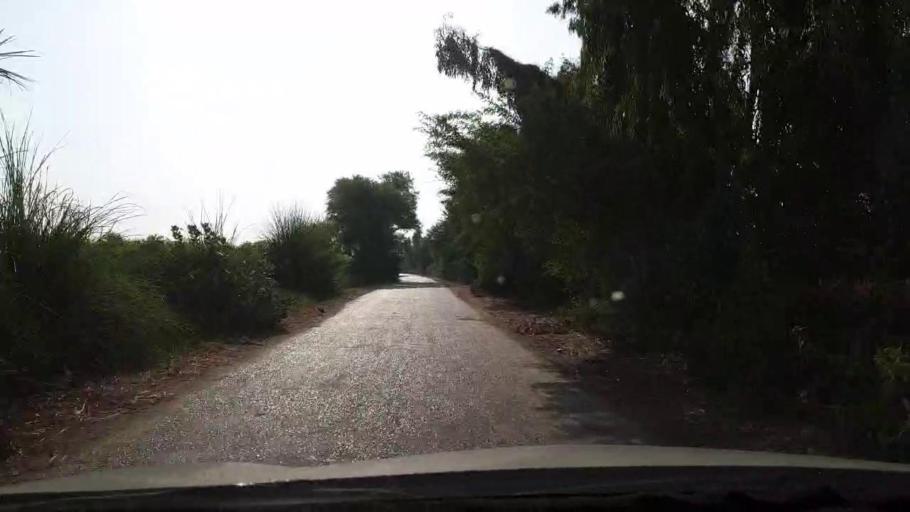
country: PK
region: Sindh
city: Larkana
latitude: 27.5497
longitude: 68.2452
